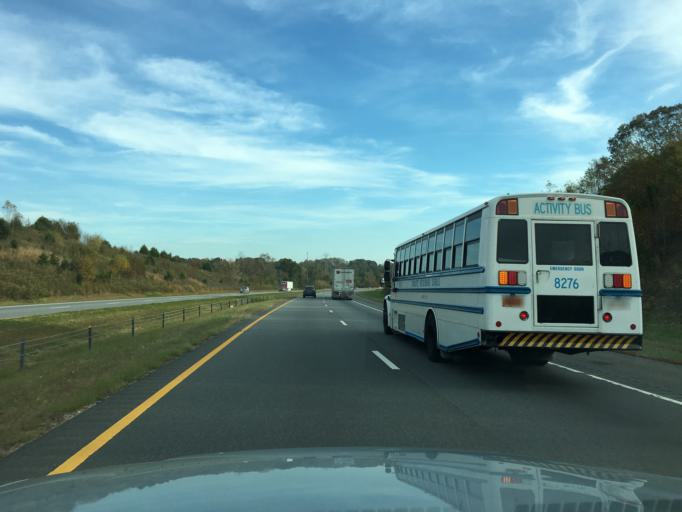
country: US
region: North Carolina
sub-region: Catawba County
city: Maiden
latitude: 35.6138
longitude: -81.2789
